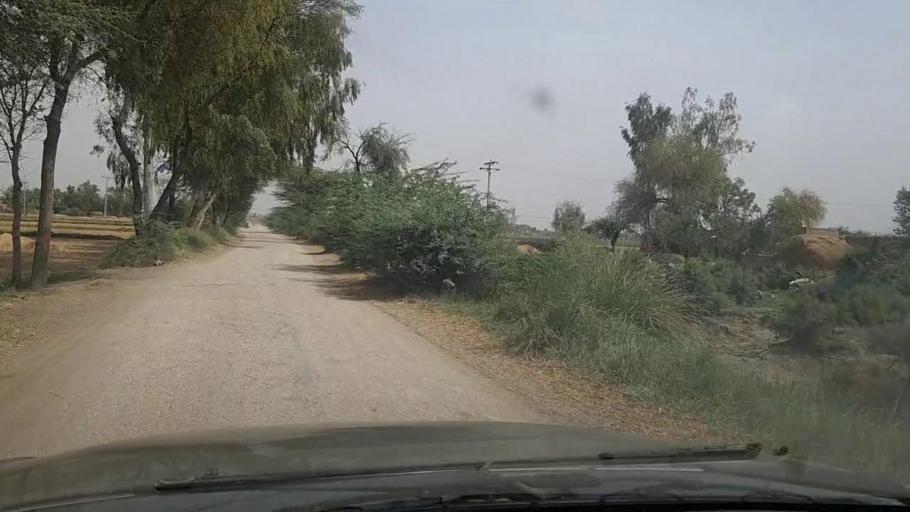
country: PK
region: Sindh
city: Shikarpur
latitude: 27.9192
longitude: 68.6804
